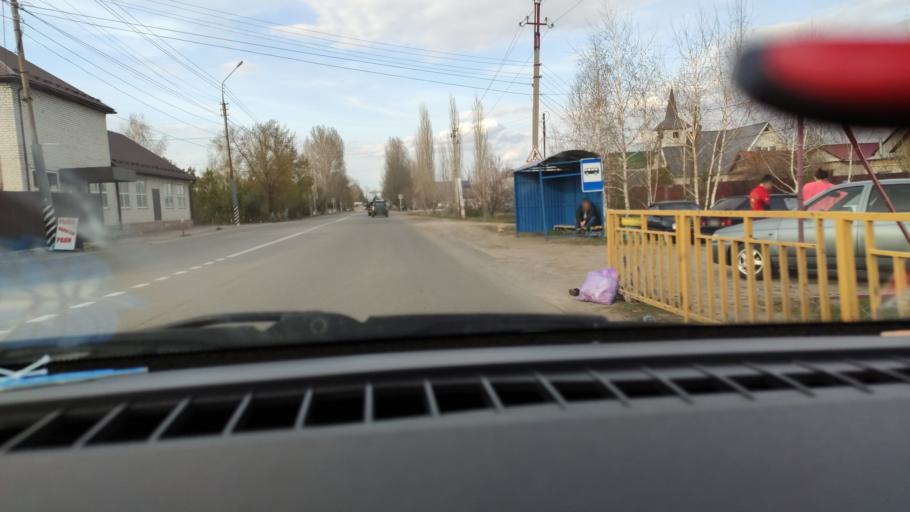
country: RU
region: Saratov
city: Privolzhskiy
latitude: 51.4342
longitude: 46.0588
